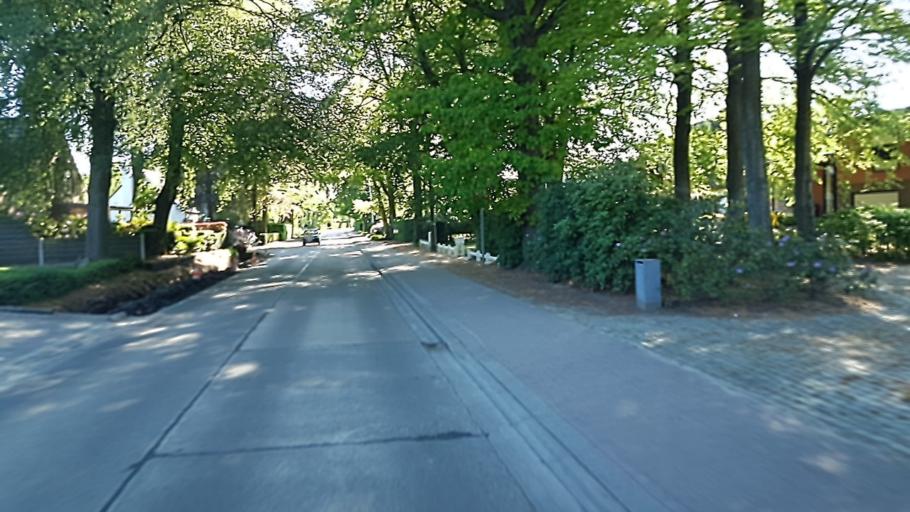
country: BE
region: Flanders
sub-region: Provincie Antwerpen
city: Heist-op-den-Berg
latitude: 51.0976
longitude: 4.7092
